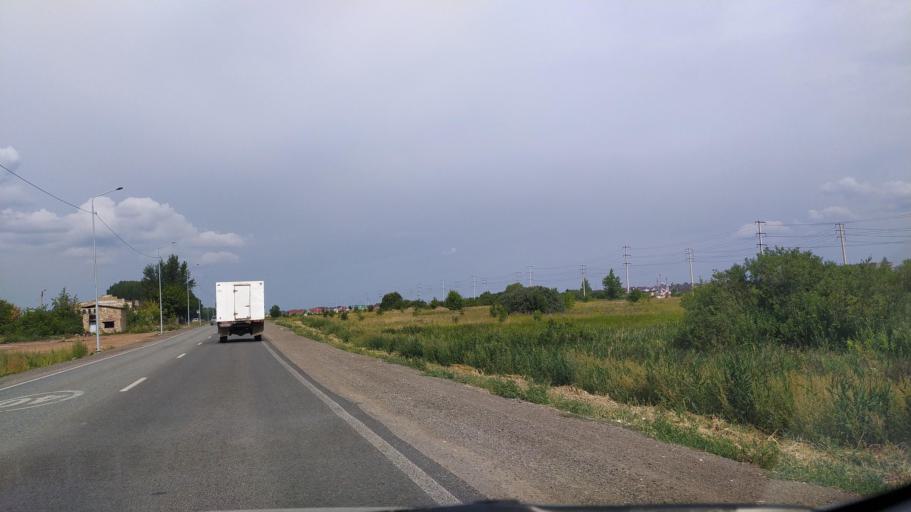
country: RU
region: Tatarstan
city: Al'met'yevsk
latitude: 54.8859
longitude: 52.2504
